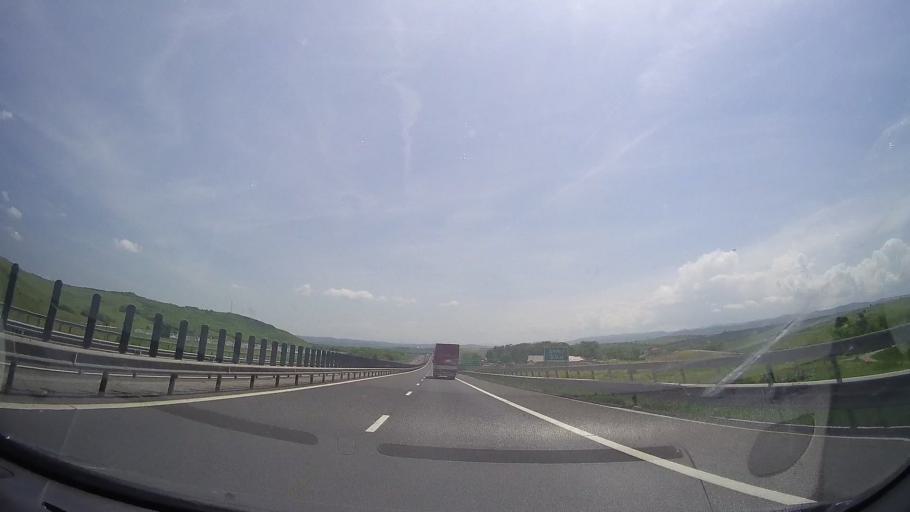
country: RO
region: Alba
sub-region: Comuna Garbova
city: Garbova
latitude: 45.9127
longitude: 23.7353
